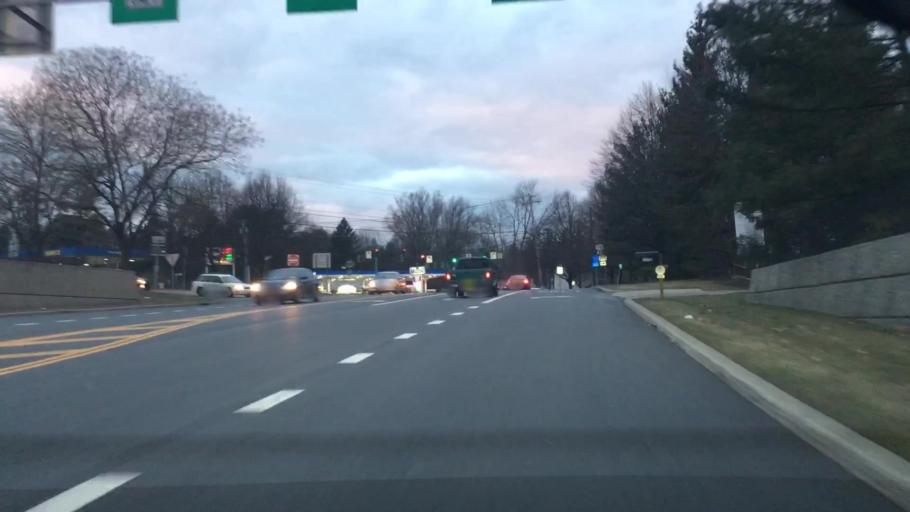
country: US
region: New York
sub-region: Dutchess County
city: Red Oaks Mill
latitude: 41.6547
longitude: -73.8739
